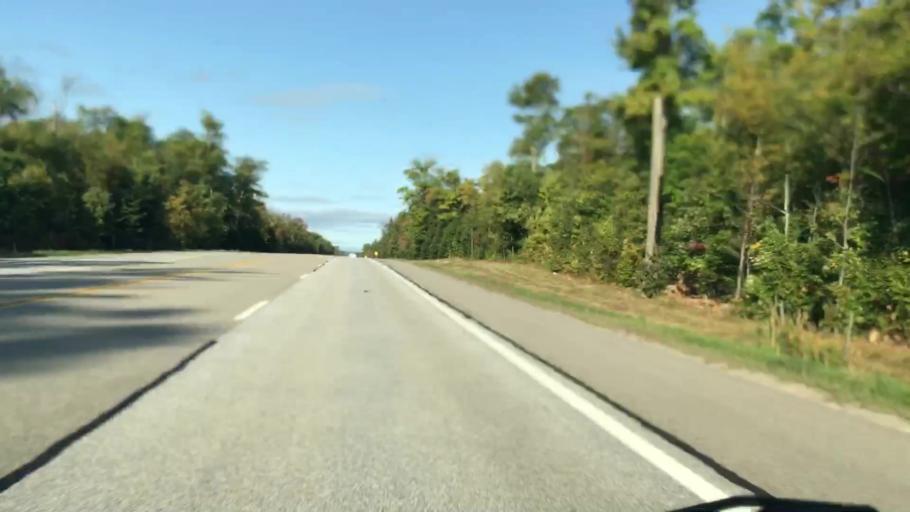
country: US
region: Michigan
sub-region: Luce County
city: Newberry
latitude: 46.3037
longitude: -85.2840
